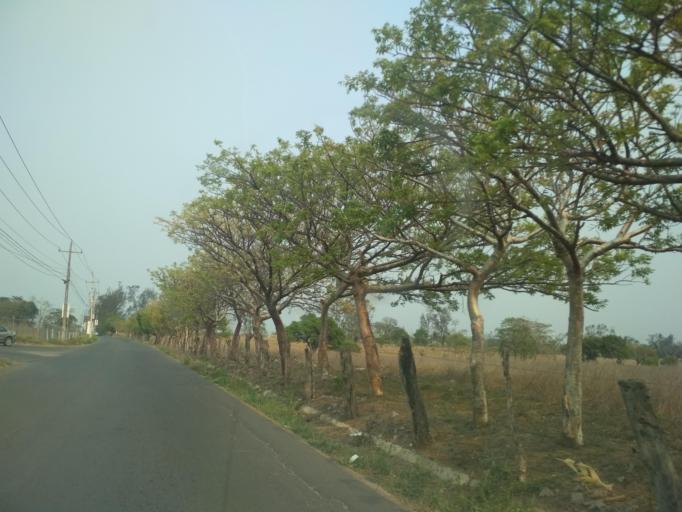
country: MX
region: Veracruz
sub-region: Veracruz
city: Las Amapolas
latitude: 19.1597
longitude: -96.2001
